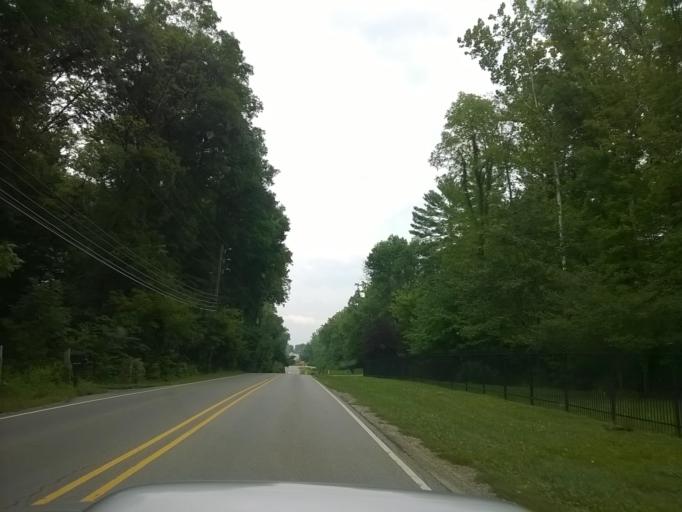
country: US
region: Indiana
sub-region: Marion County
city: Meridian Hills
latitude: 39.9415
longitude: -86.1697
